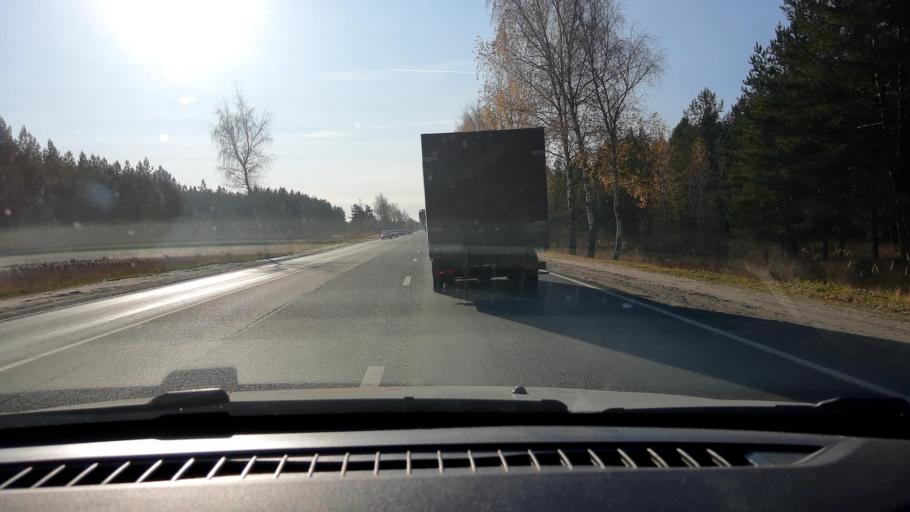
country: RU
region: Nizjnij Novgorod
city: Dzerzhinsk
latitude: 56.2878
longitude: 43.4757
